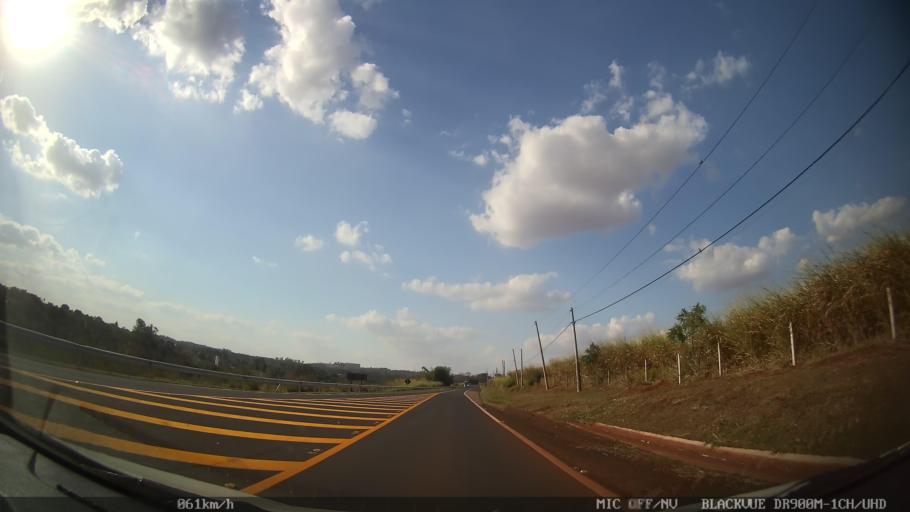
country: BR
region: Sao Paulo
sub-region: Ribeirao Preto
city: Ribeirao Preto
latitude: -21.1879
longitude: -47.8640
